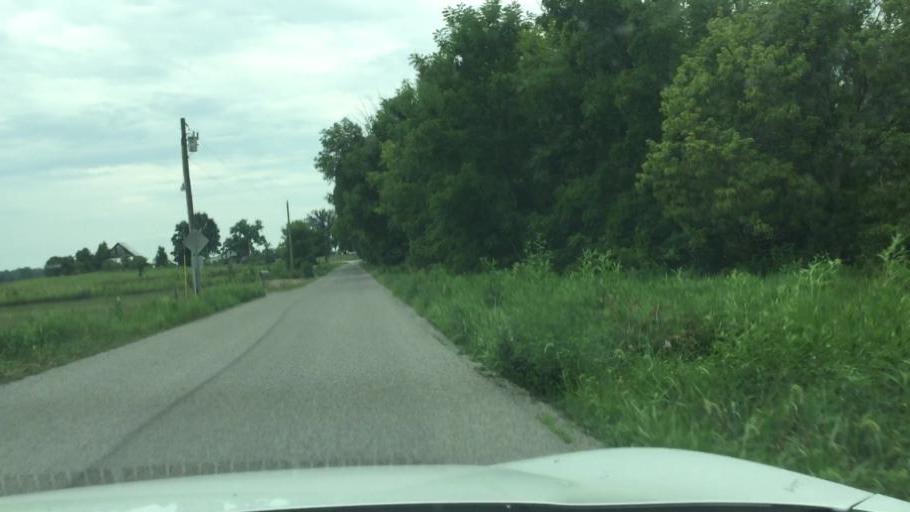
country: US
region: Ohio
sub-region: Champaign County
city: North Lewisburg
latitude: 40.2447
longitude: -83.5233
